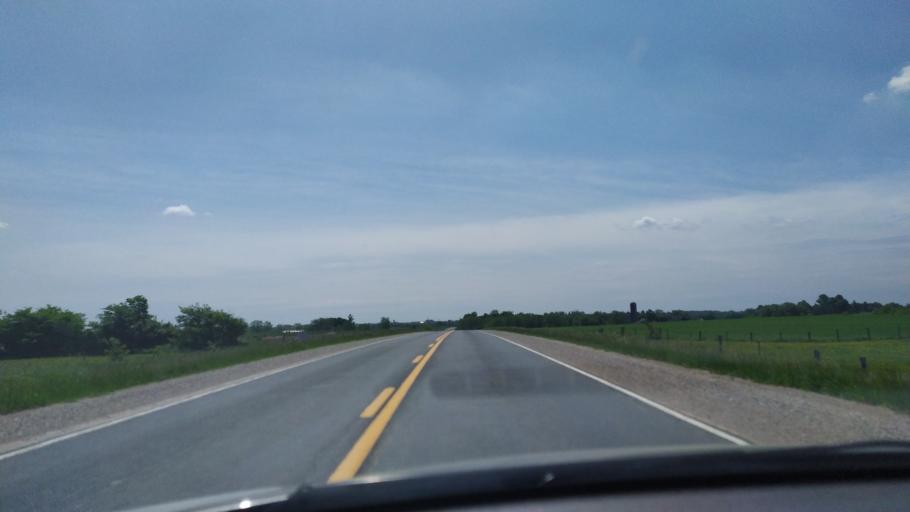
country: CA
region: Ontario
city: Ingersoll
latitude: 43.0203
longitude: -80.9674
